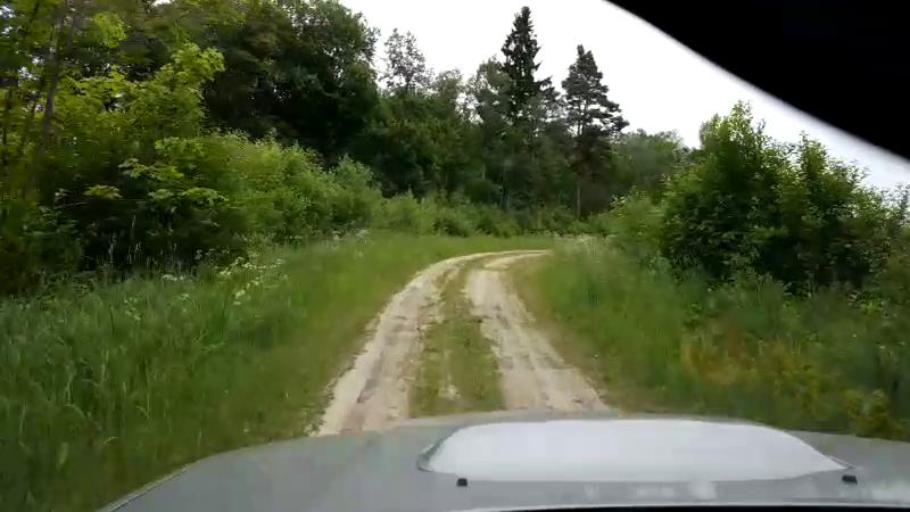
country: EE
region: Paernumaa
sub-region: Halinga vald
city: Parnu-Jaagupi
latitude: 58.5366
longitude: 24.6161
